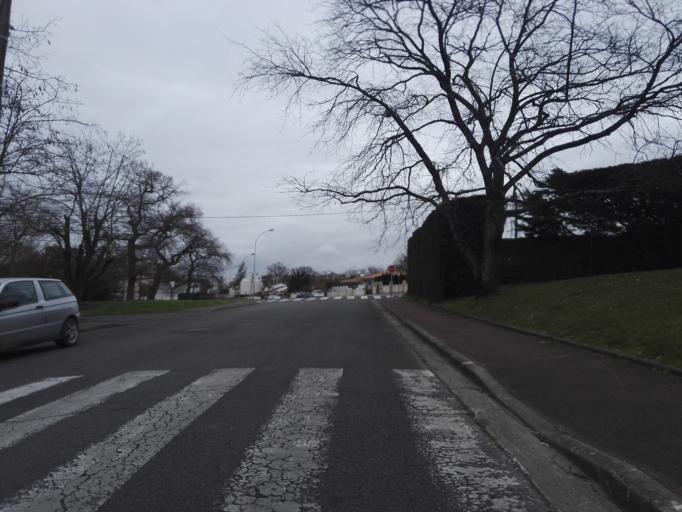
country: FR
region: Aquitaine
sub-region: Departement de la Gironde
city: Talence
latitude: 44.8016
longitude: -0.5816
